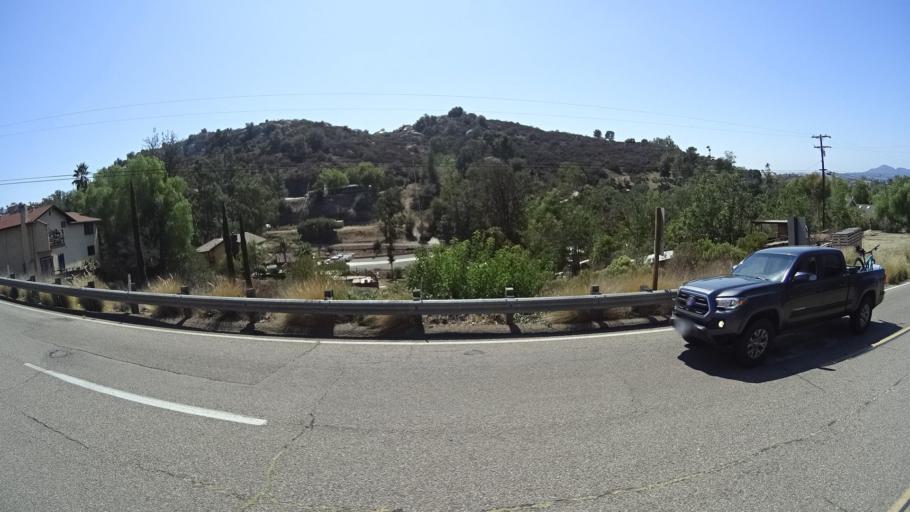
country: US
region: California
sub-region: San Diego County
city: Granite Hills
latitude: 32.8114
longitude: -116.9015
